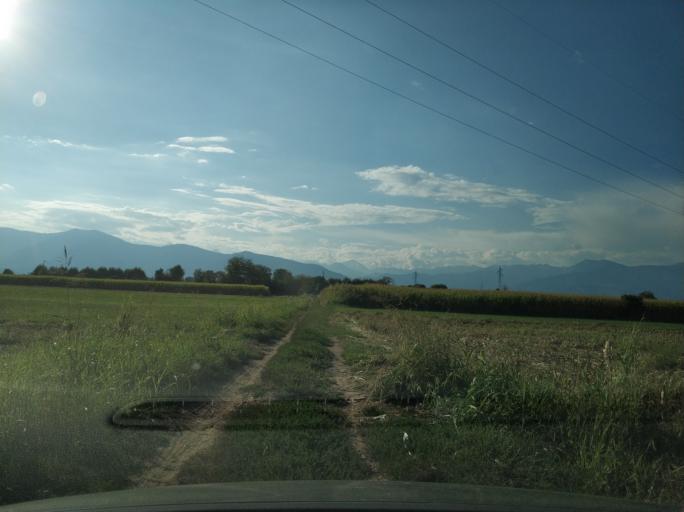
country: IT
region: Piedmont
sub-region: Provincia di Torino
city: Cirie
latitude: 45.2076
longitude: 7.6060
